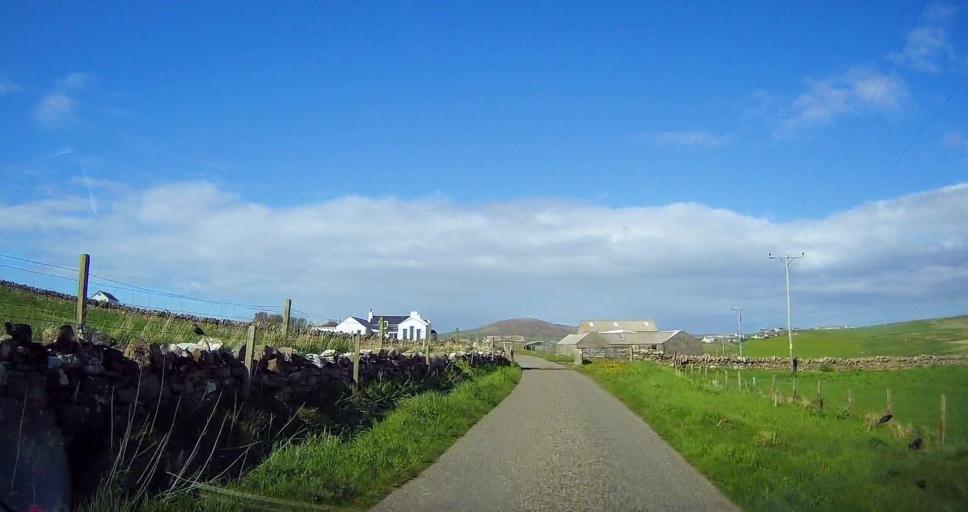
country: GB
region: Scotland
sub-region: Shetland Islands
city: Sandwick
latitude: 59.9060
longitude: -1.3352
